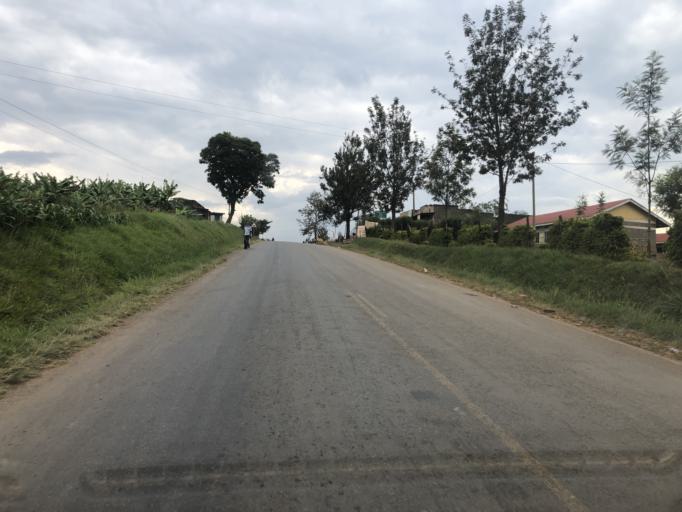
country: UG
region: Western Region
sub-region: Sheema District
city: Kibingo
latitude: -0.5789
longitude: 30.4091
